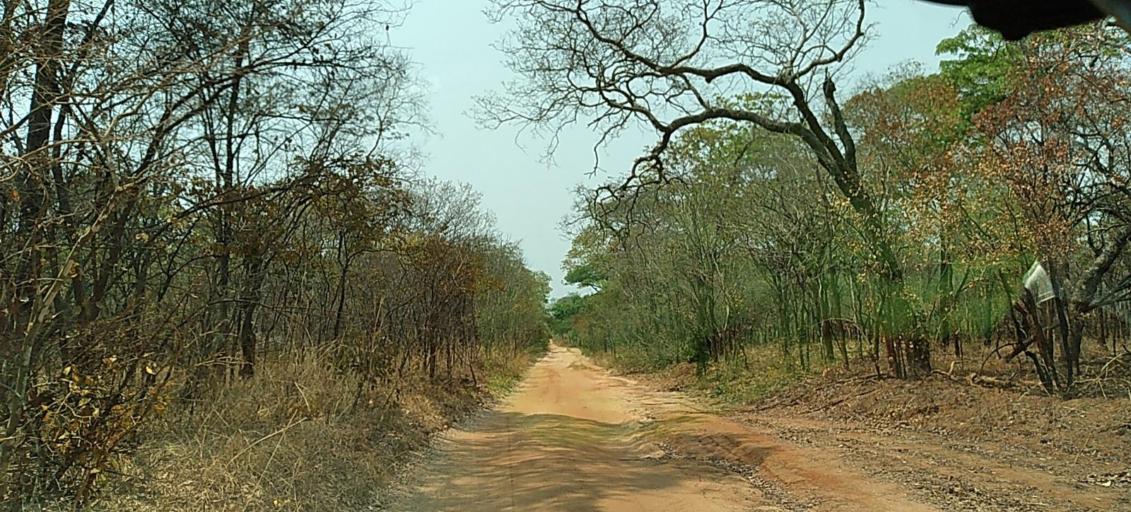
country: ZM
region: North-Western
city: Kabompo
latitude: -13.6905
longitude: 24.3069
